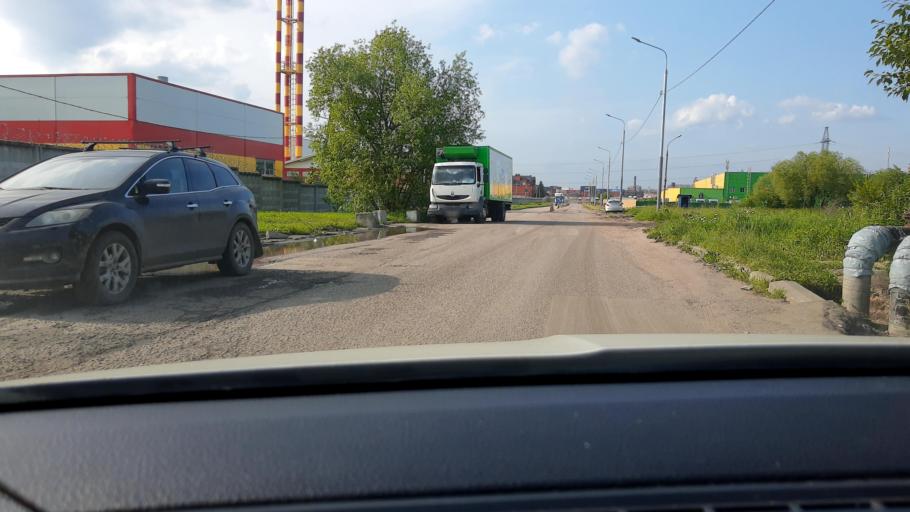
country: RU
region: Moskovskaya
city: Shcherbinka
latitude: 55.4829
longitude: 37.5633
